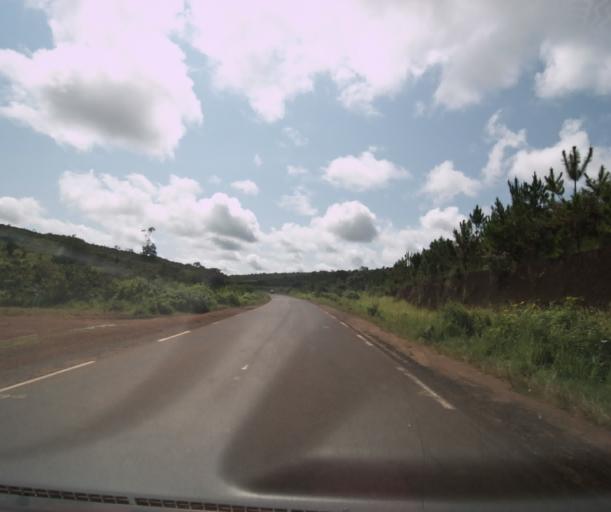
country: CM
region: West
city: Foumban
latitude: 5.7039
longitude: 10.8391
